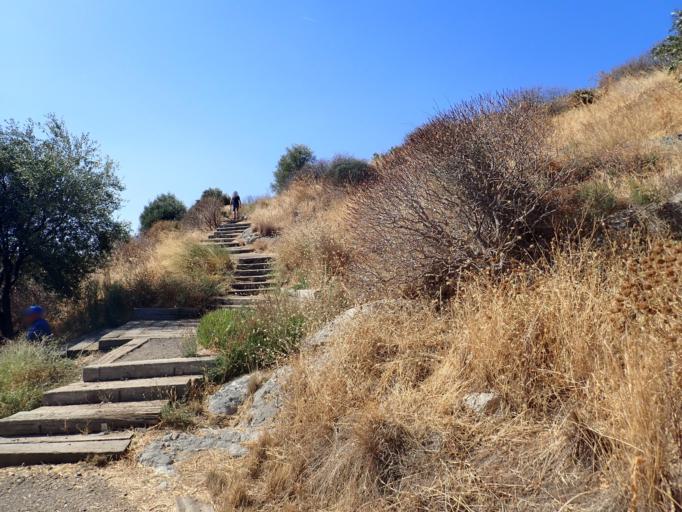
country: GR
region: Peloponnese
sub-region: Nomos Argolidos
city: Tolon
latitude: 37.5273
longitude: 22.8750
